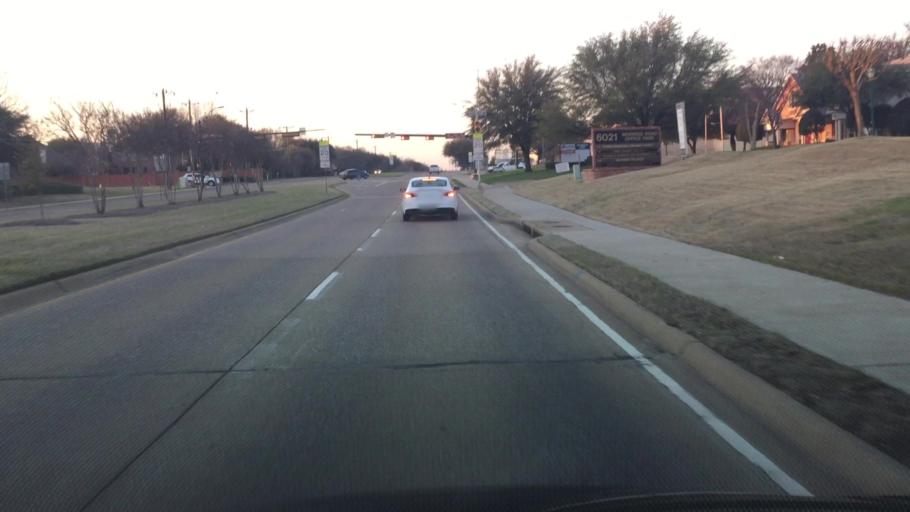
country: US
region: Texas
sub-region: Denton County
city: Highland Village
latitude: 33.0675
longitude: -97.0619
